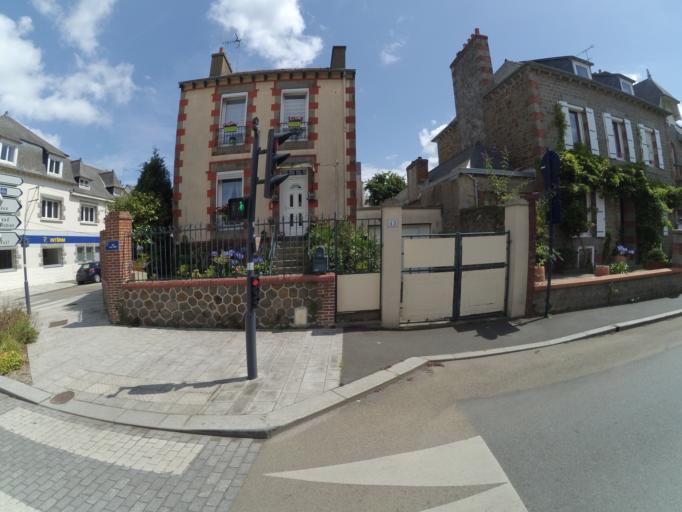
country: FR
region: Brittany
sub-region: Departement des Cotes-d'Armor
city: Saint-Brieuc
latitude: 48.5046
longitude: -2.7673
